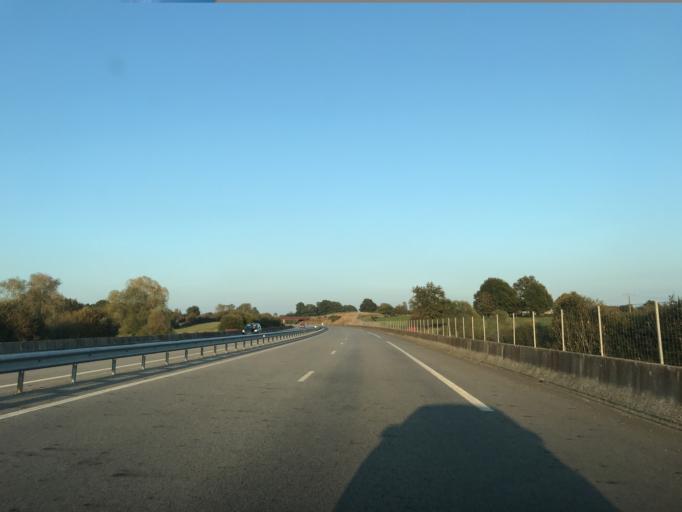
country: FR
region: Lower Normandy
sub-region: Departement de l'Orne
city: Sees
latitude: 48.4875
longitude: 0.2875
